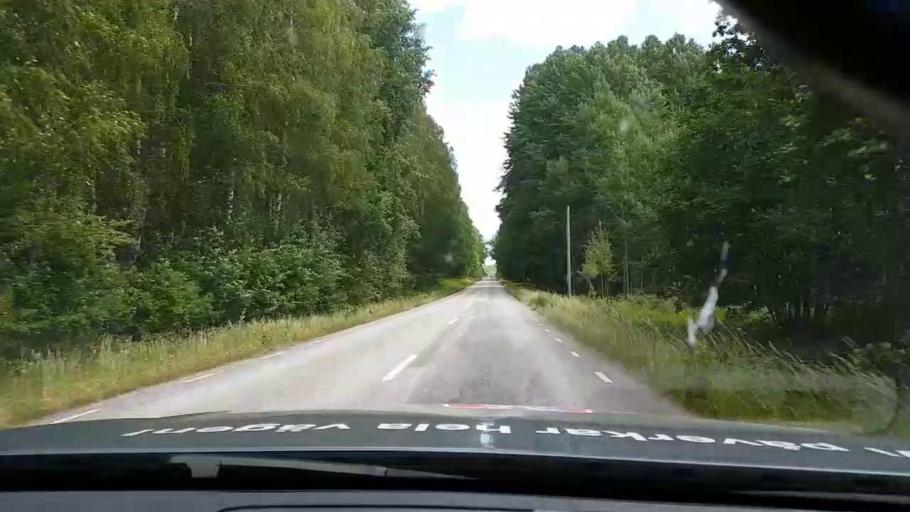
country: SE
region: Kalmar
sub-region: Vasterviks Kommun
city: Forserum
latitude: 58.0394
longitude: 16.4348
